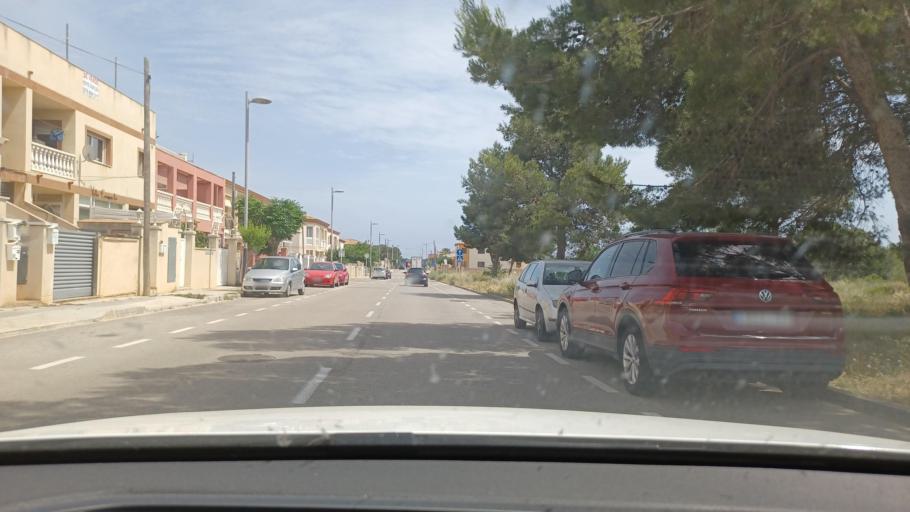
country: ES
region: Catalonia
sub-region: Provincia de Tarragona
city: Colldejou
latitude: 41.0029
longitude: 0.9264
